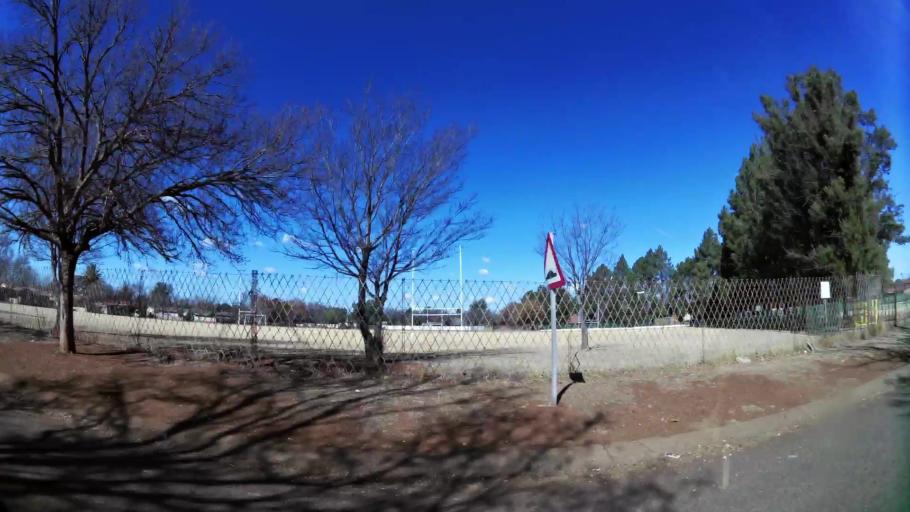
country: ZA
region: Gauteng
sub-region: West Rand District Municipality
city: Carletonville
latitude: -26.3644
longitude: 27.3816
